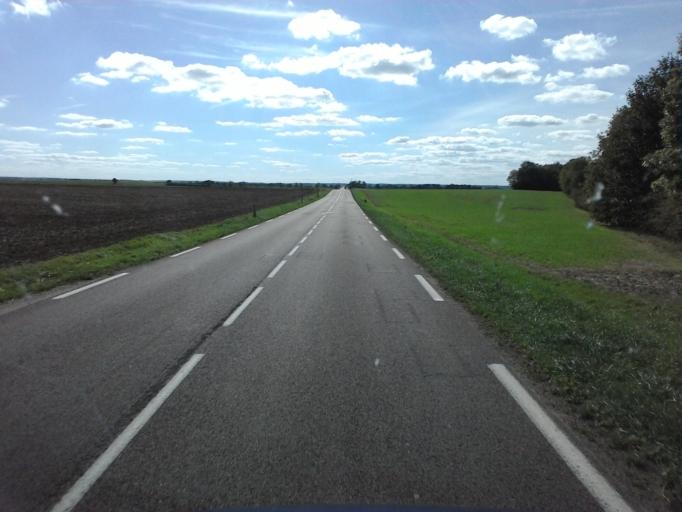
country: FR
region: Bourgogne
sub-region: Departement de la Cote-d'Or
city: Chatillon-sur-Seine
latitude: 47.8928
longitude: 4.6071
